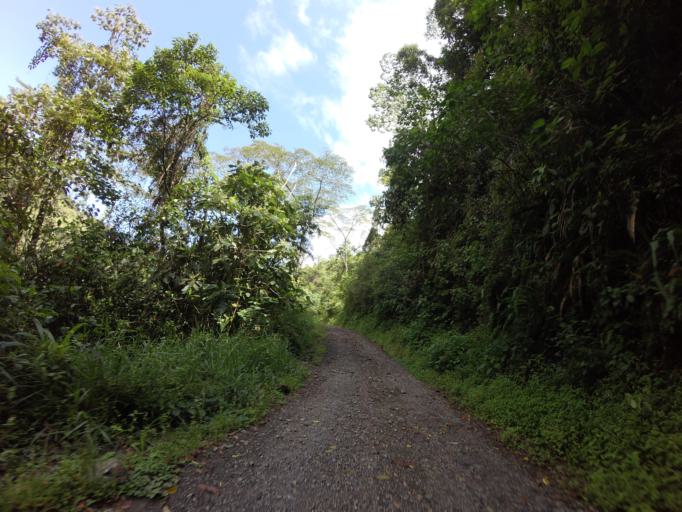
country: CO
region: Caldas
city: Pensilvania
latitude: 5.4541
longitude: -75.1802
